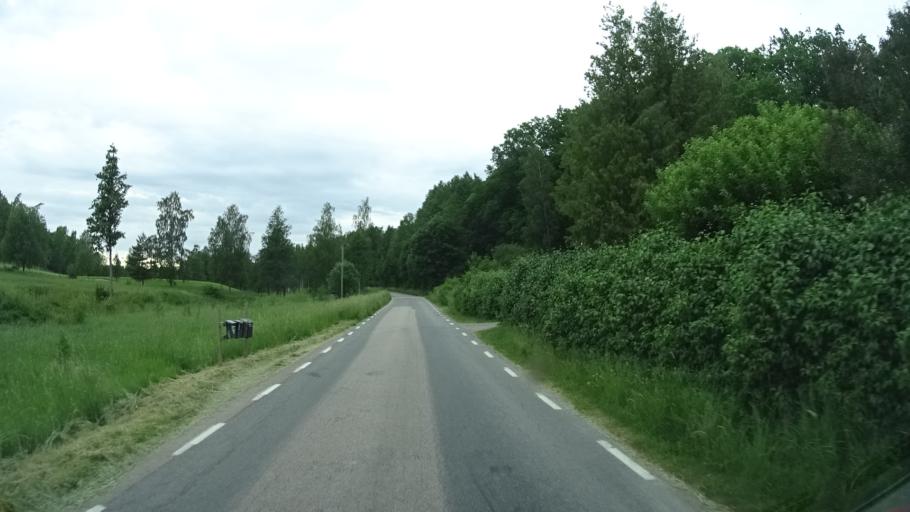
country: SE
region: Soedermanland
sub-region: Nykopings Kommun
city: Stigtomta
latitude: 58.7534
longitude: 16.7227
